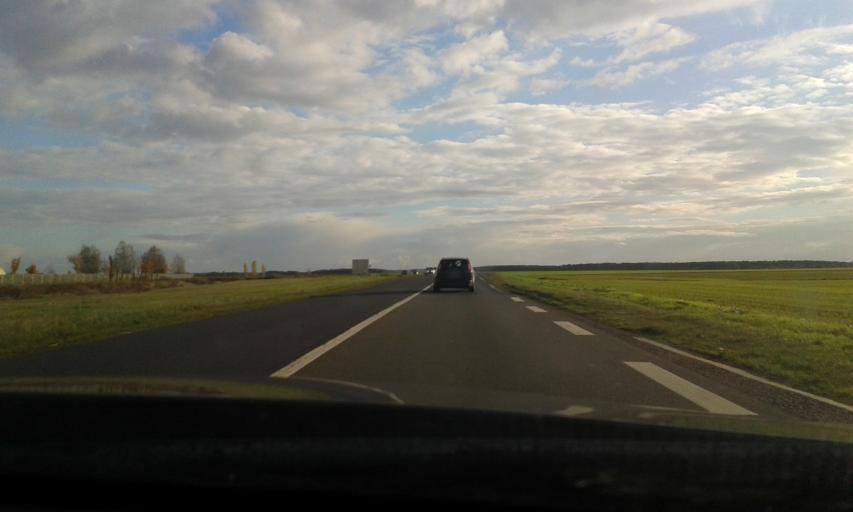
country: FR
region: Centre
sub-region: Departement d'Eure-et-Loir
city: Vernouillet
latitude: 48.7103
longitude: 1.3693
